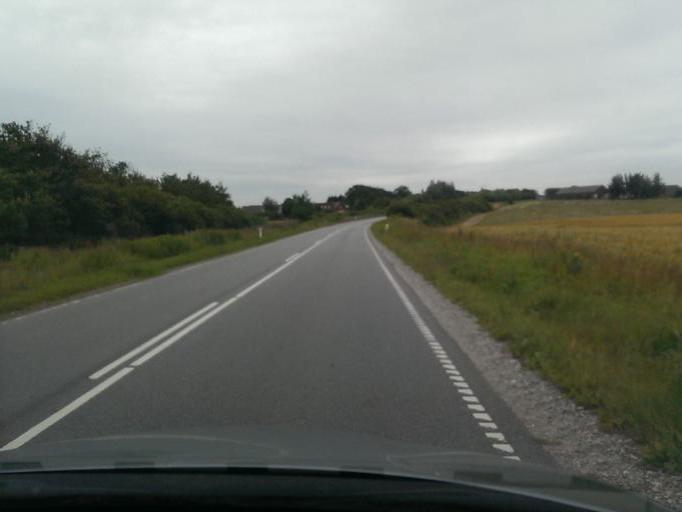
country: DK
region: North Denmark
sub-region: Hjorring Kommune
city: Vra
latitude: 57.3542
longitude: 9.9170
